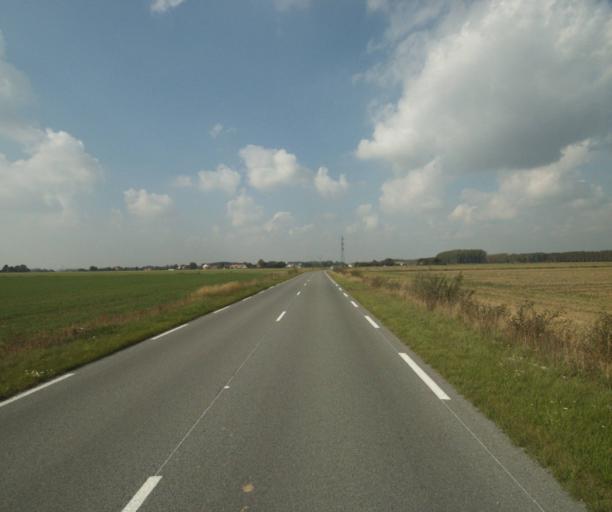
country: FR
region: Nord-Pas-de-Calais
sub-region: Departement du Nord
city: Houplin-Ancoisne
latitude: 50.5722
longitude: 3.0093
